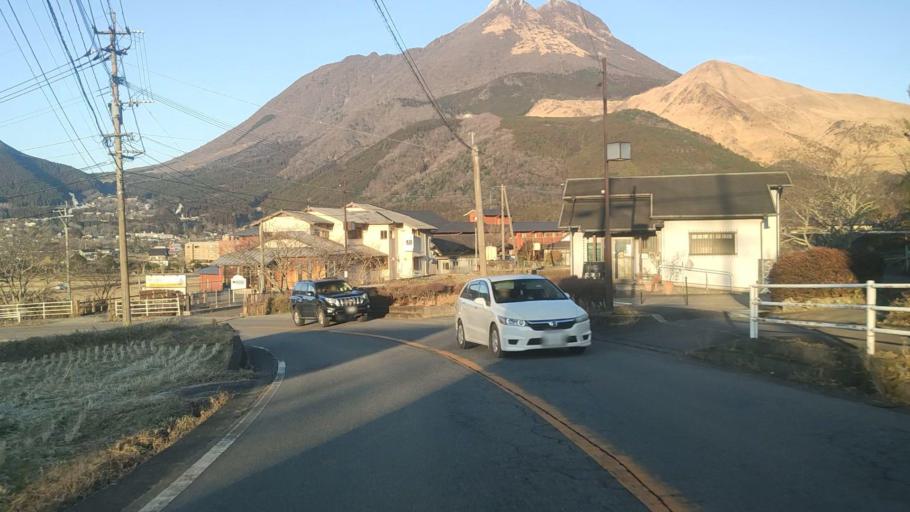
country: JP
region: Oita
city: Beppu
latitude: 33.2559
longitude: 131.3594
